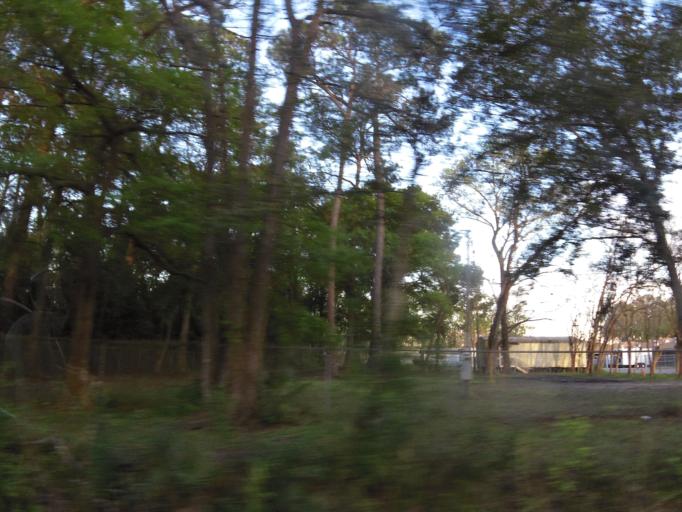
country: US
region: Florida
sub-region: Duval County
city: Jacksonville
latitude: 30.3429
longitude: -81.7292
